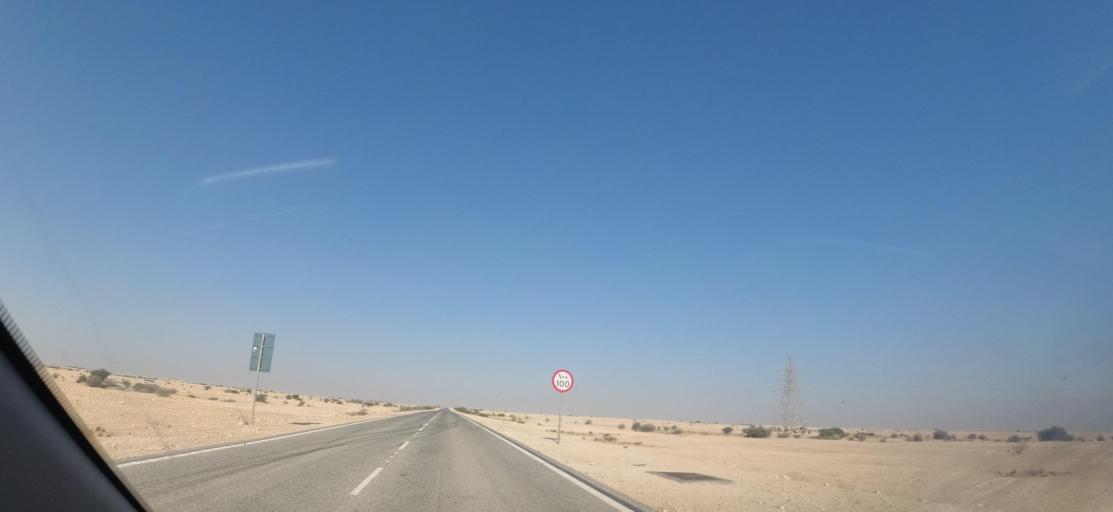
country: QA
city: Al Jumayliyah
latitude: 25.6320
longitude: 51.0961
